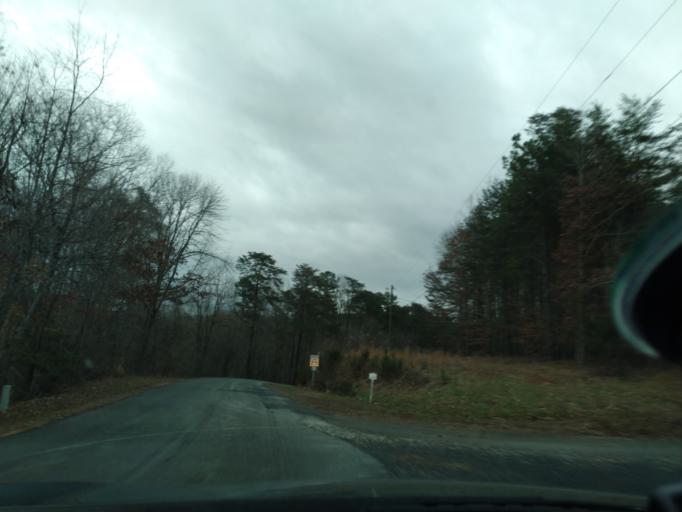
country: US
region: Virginia
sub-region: Buckingham County
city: Buckingham
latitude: 37.3914
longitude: -78.6439
